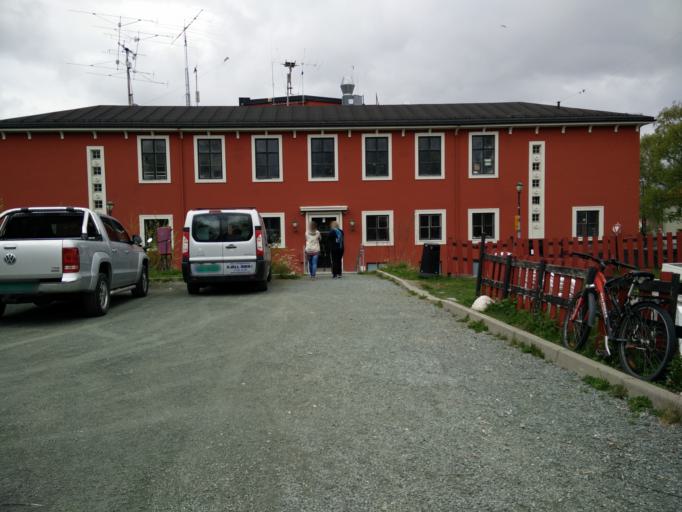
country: NO
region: Sor-Trondelag
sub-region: Trondheim
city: Trondheim
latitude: 63.4222
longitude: 10.3966
